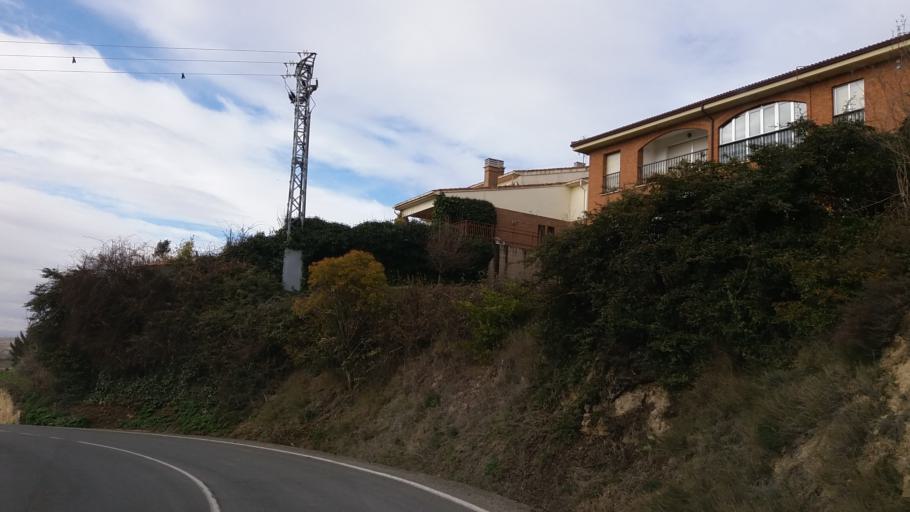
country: ES
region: La Rioja
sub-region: Provincia de La Rioja
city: San Vicente de la Sonsierra
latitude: 42.5641
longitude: -2.7613
